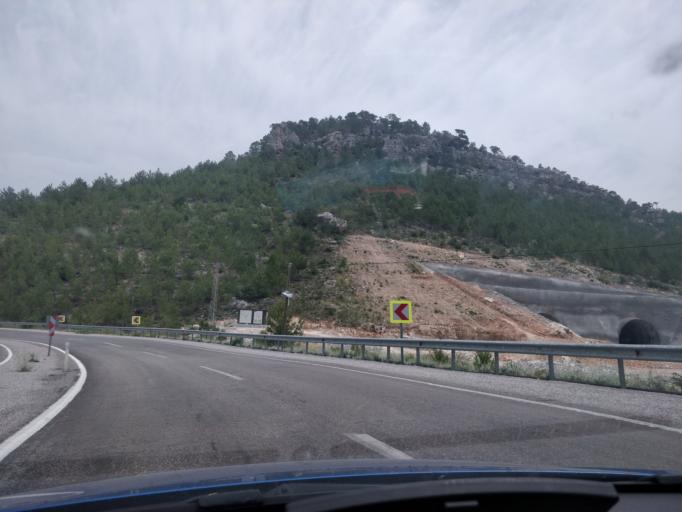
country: TR
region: Mersin
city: Tasucu
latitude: 36.3967
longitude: 33.8502
